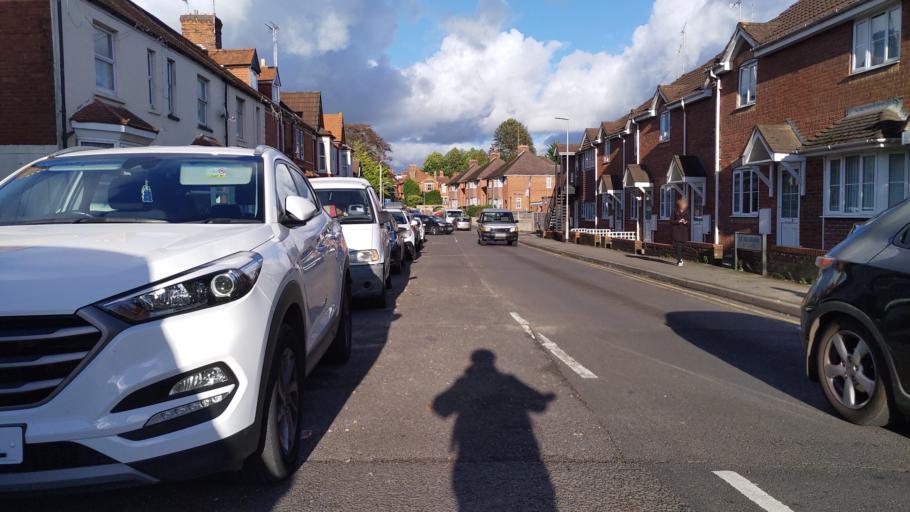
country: GB
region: England
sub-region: Somerset
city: Yeovil
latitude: 50.9382
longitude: -2.6412
